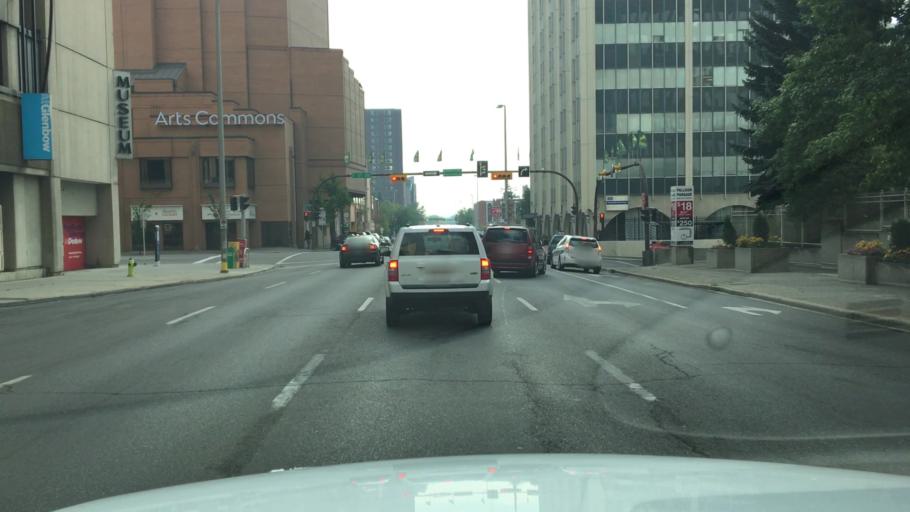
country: CA
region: Alberta
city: Calgary
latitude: 51.0445
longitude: -114.0613
